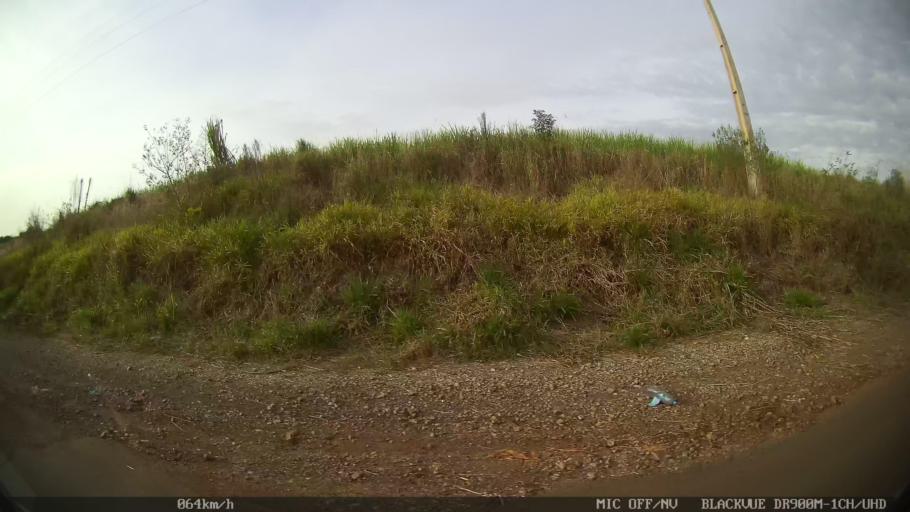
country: BR
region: Sao Paulo
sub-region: Piracicaba
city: Piracicaba
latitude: -22.7068
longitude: -47.5830
